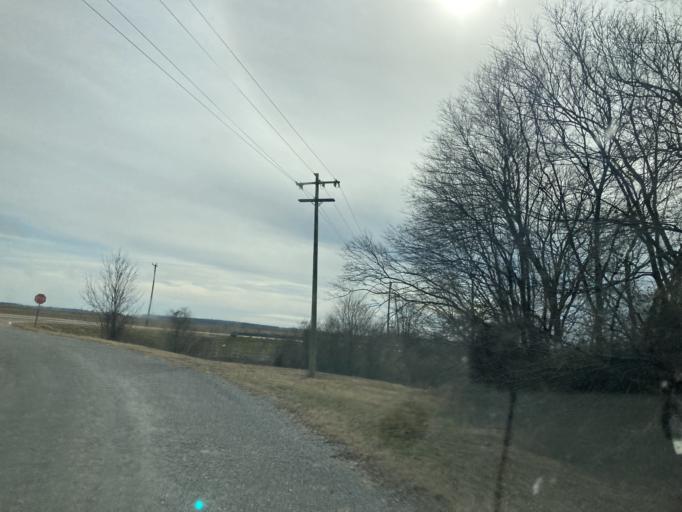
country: US
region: Mississippi
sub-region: Humphreys County
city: Belzoni
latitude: 33.1833
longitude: -90.6329
